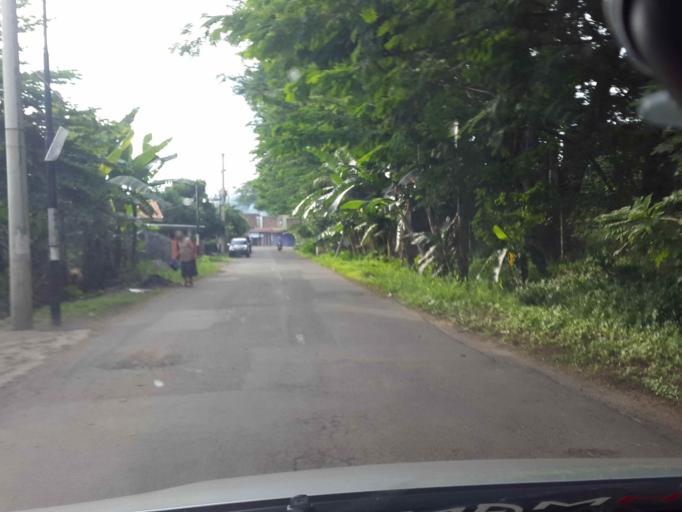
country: ID
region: Banten
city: Curug
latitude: -5.9965
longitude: 106.0562
